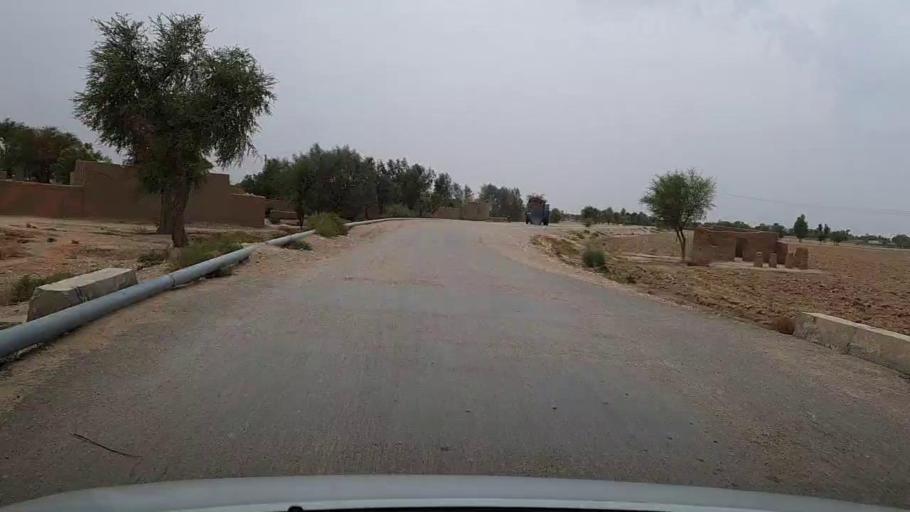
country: PK
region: Sindh
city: Sehwan
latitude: 26.3194
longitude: 67.7347
